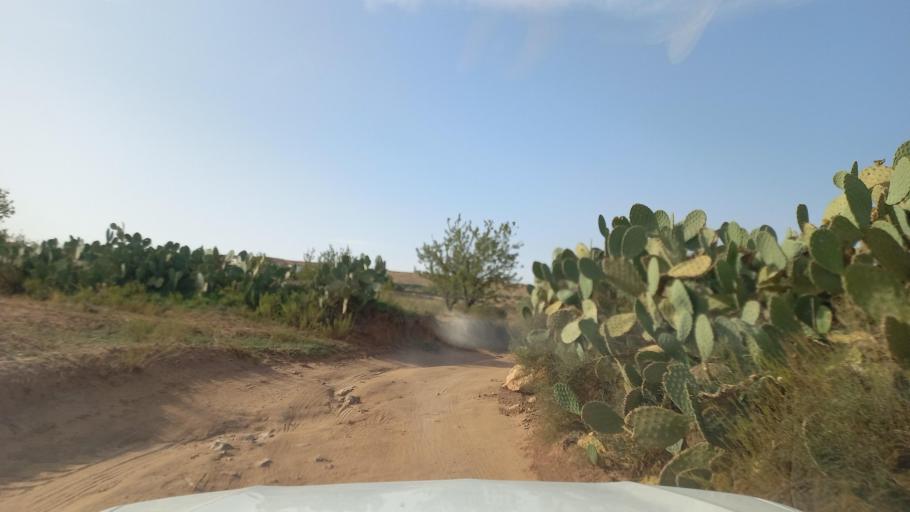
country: TN
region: Al Qasrayn
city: Kasserine
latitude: 35.3621
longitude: 8.8502
